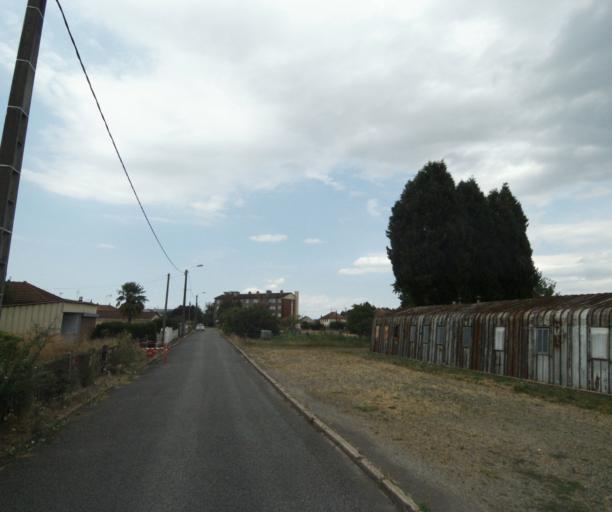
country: FR
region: Bourgogne
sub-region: Departement de Saone-et-Loire
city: Gueugnon
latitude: 46.6054
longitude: 4.0589
